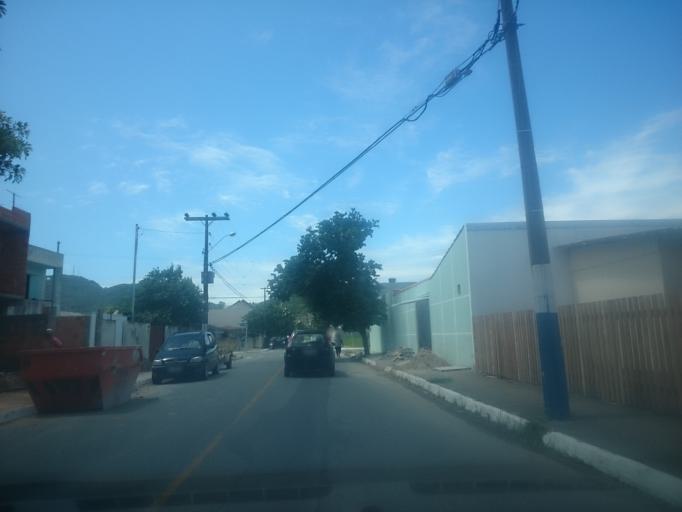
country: BR
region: Santa Catarina
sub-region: Balneario Camboriu
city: Balneario Camboriu
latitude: -27.0246
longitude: -48.6132
